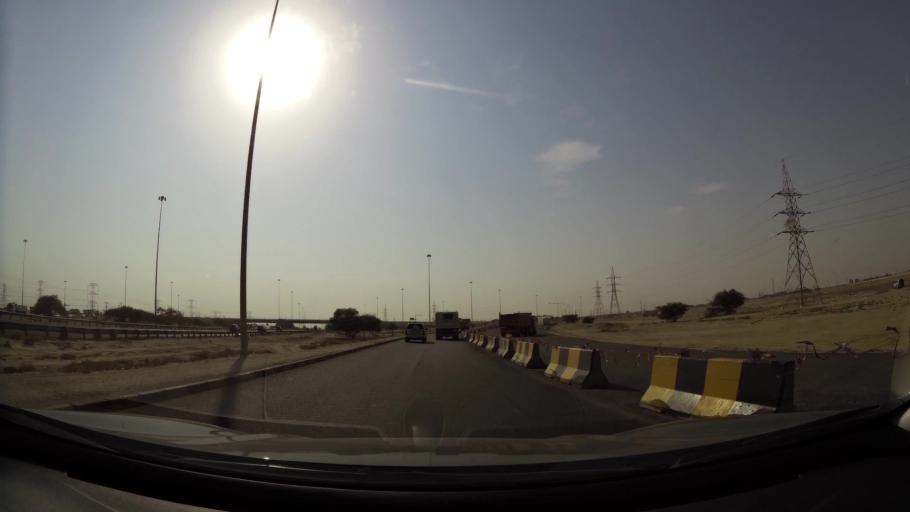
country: KW
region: Al Ahmadi
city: Al Ahmadi
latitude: 28.9617
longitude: 48.1197
